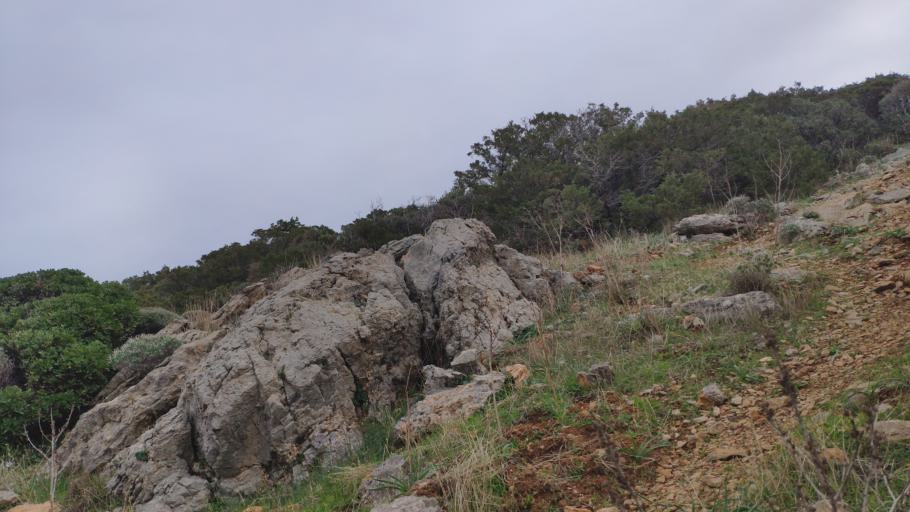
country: GR
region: Attica
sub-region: Nomarchia Anatolikis Attikis
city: Limin Mesoyaias
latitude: 37.9058
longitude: 24.0420
